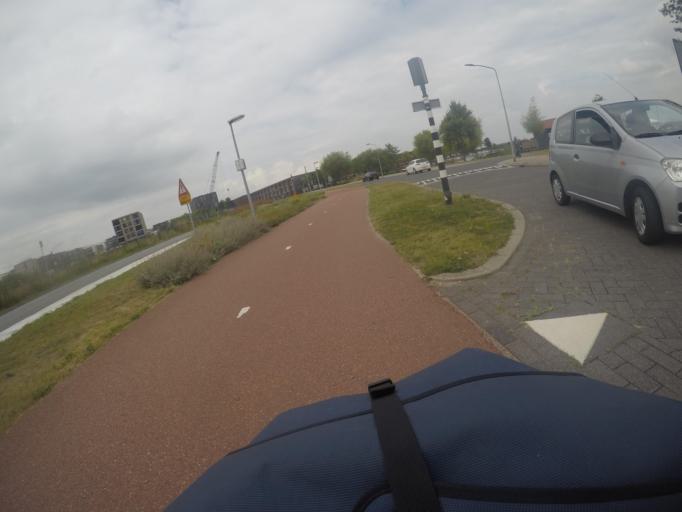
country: NL
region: Flevoland
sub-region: Gemeente Almere
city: Almere Stad
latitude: 52.3905
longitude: 5.1787
